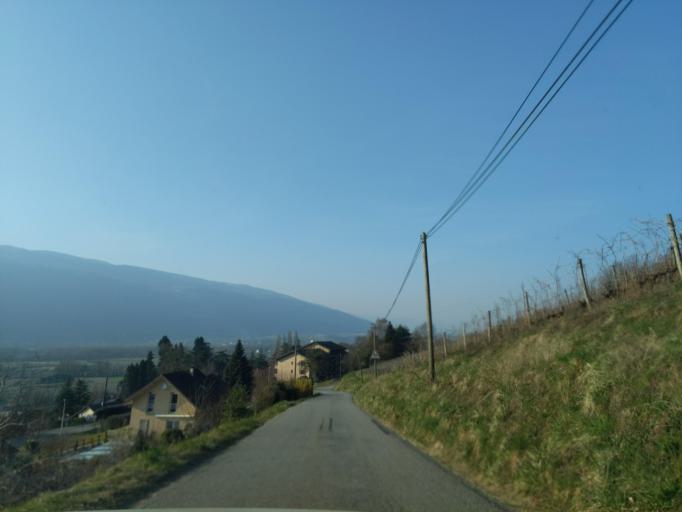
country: FR
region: Rhone-Alpes
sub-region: Departement de la Savoie
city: Chindrieux
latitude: 45.8840
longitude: 5.8471
